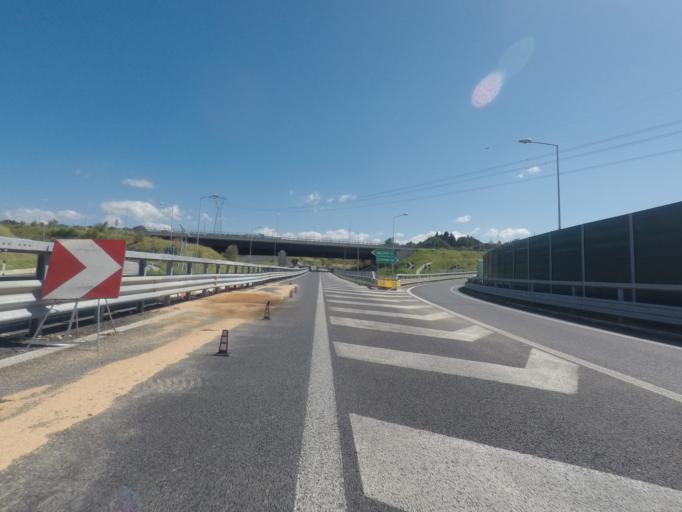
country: IT
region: Calabria
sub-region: Provincia di Reggio Calabria
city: Campo Calabro
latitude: 38.2048
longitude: 15.6390
